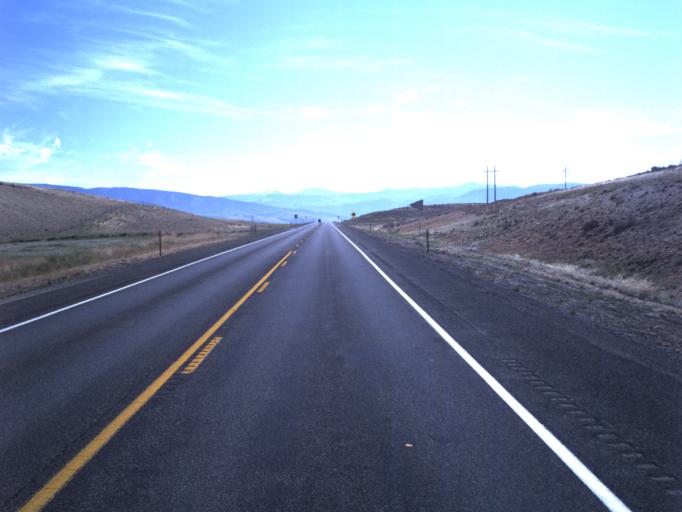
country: US
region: Utah
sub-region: Sanpete County
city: Gunnison
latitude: 39.1723
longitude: -111.8325
